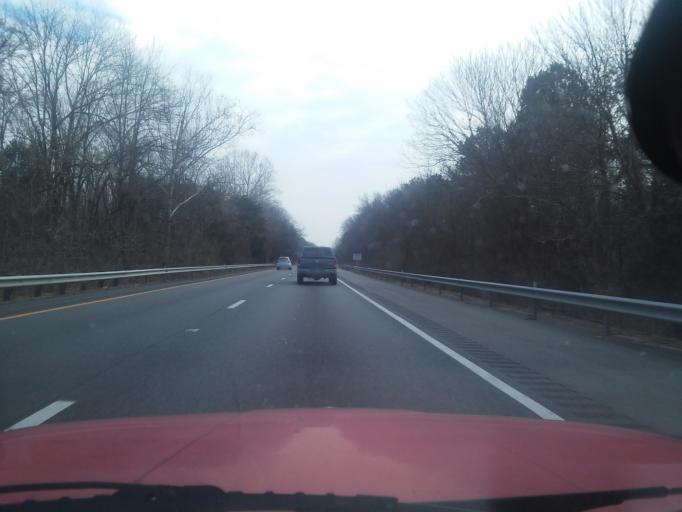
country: US
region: Virginia
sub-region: Fluvanna County
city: Lake Monticello
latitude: 38.0099
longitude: -78.3741
